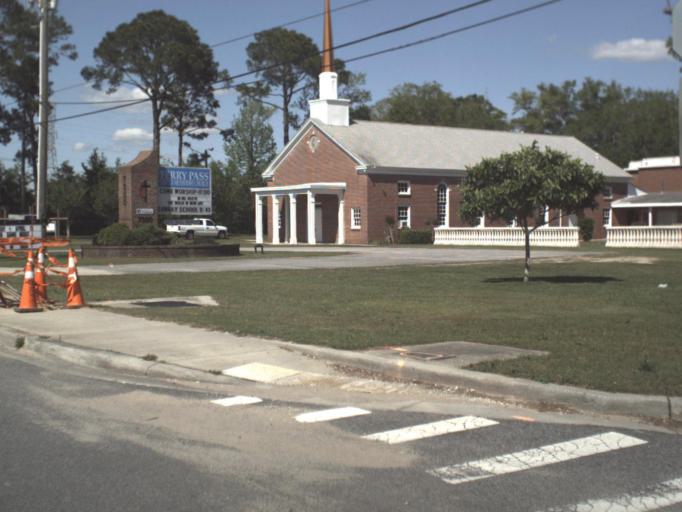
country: US
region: Florida
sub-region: Escambia County
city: Ferry Pass
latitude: 30.5007
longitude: -87.2216
